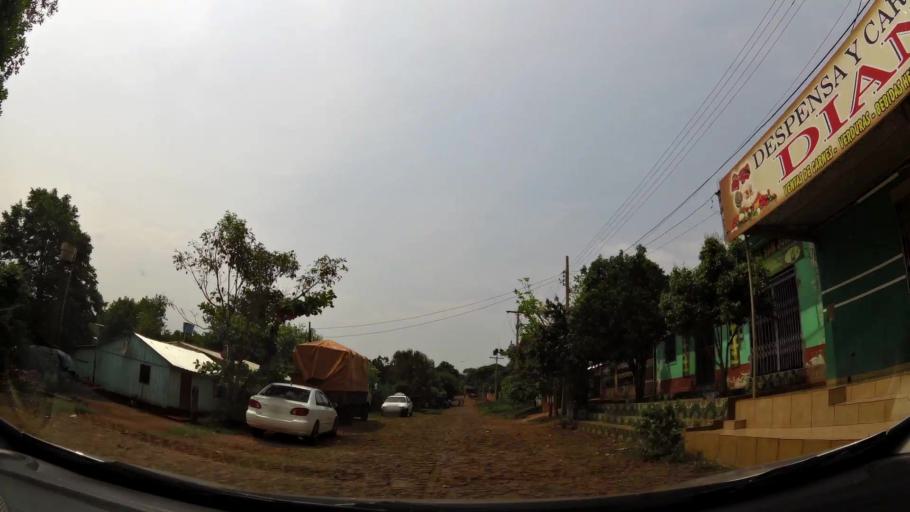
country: BR
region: Parana
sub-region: Foz Do Iguacu
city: Foz do Iguacu
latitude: -25.5706
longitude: -54.6164
